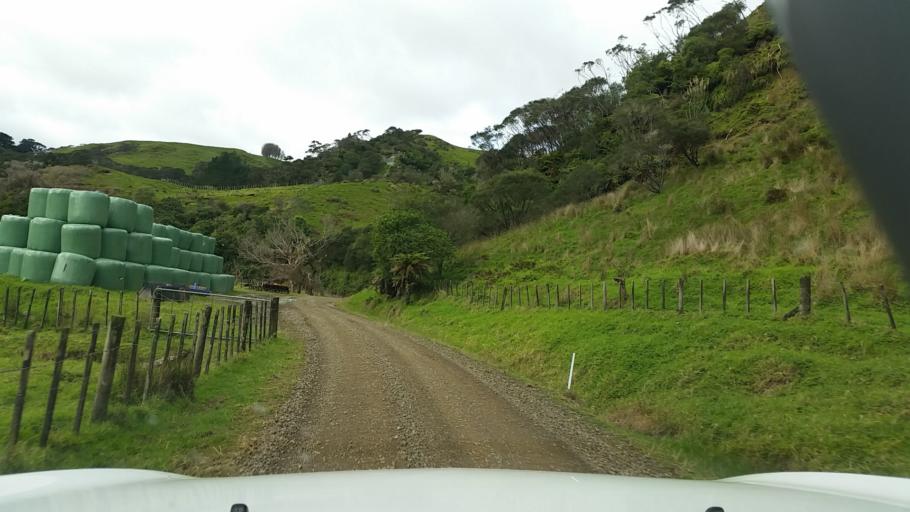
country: NZ
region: Taranaki
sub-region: New Plymouth District
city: Waitara
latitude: -38.8628
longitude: 174.6591
